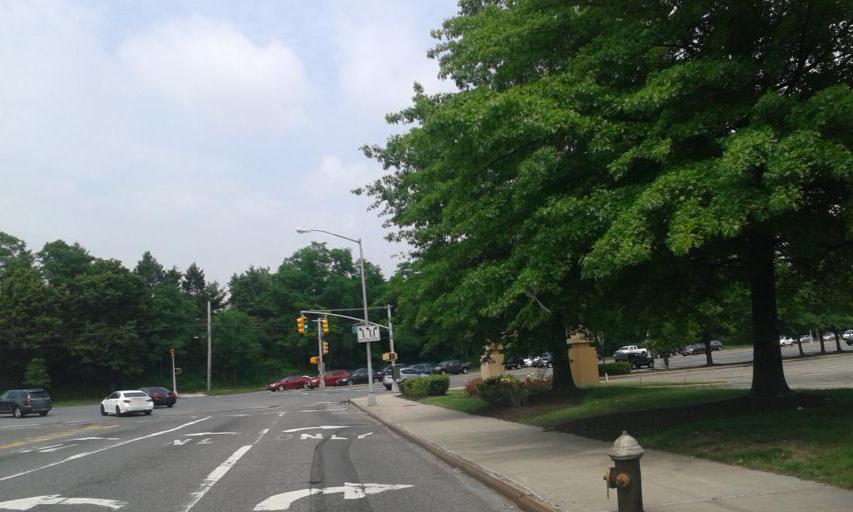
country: US
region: New York
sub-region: Richmond County
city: Staten Island
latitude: 40.5791
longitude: -74.1685
